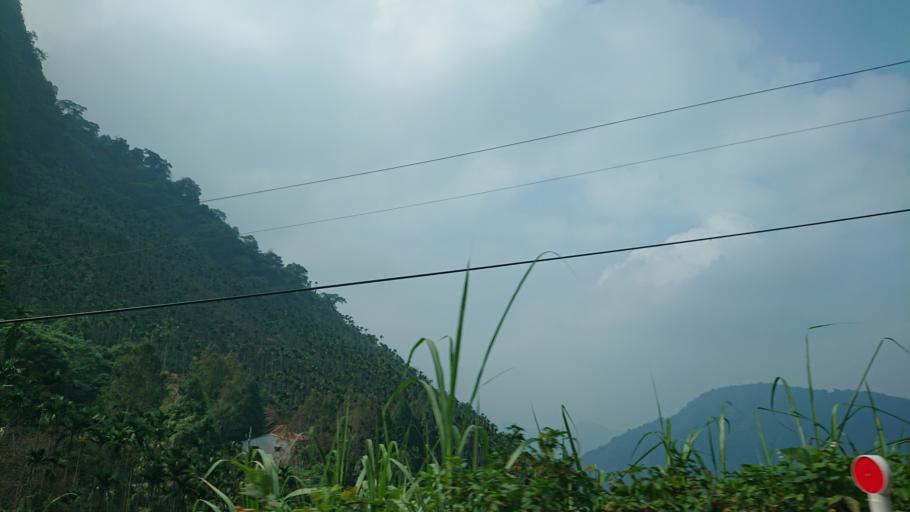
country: TW
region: Taiwan
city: Lugu
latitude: 23.5962
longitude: 120.6889
